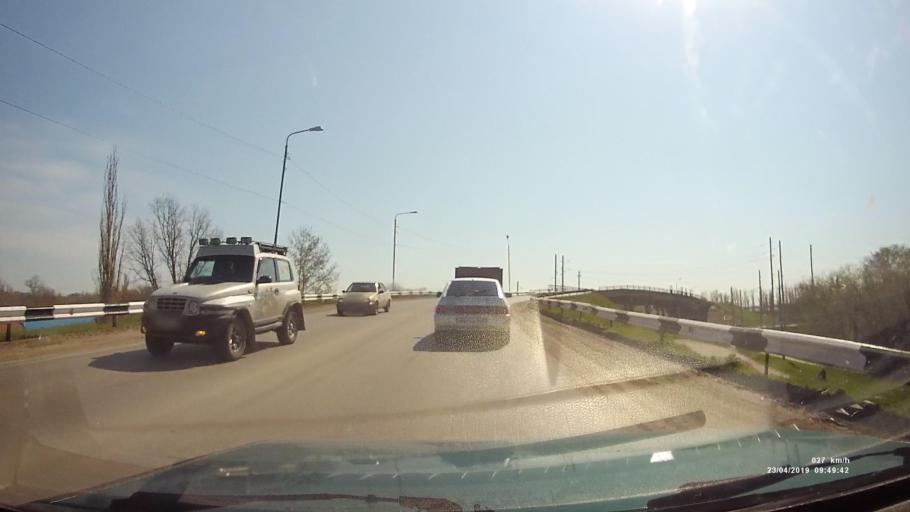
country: RU
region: Rostov
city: Orlovskiy
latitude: 46.8646
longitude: 42.0346
